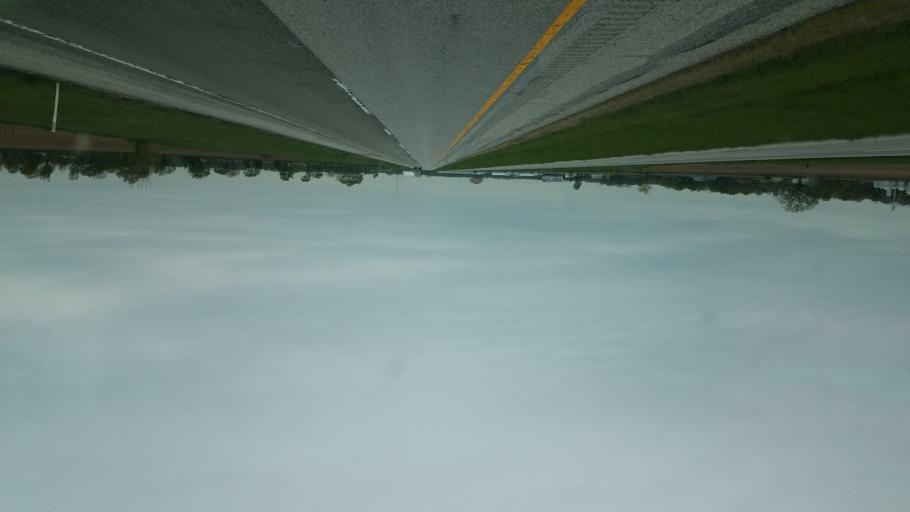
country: US
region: Michigan
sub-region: Saint Joseph County
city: Sturgis
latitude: 41.7456
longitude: -85.5204
